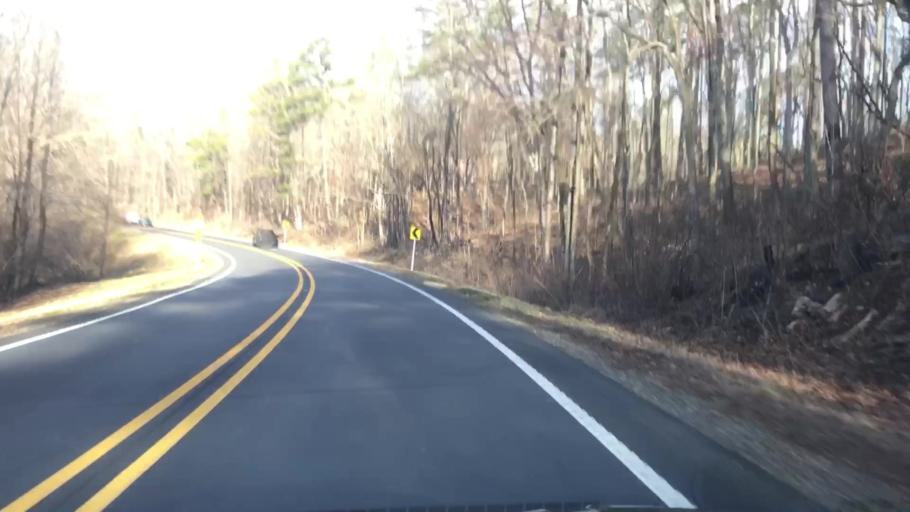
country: US
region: Arkansas
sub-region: Montgomery County
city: Mount Ida
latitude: 34.5226
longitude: -93.3913
